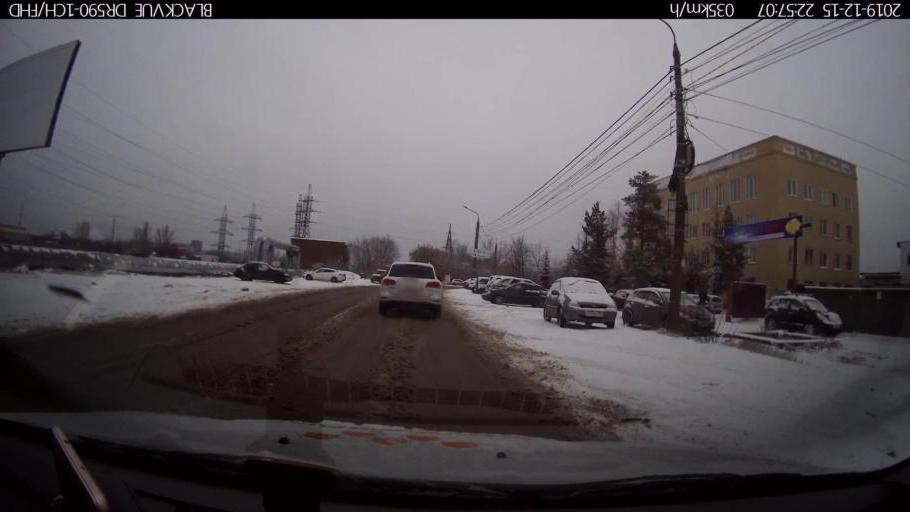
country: RU
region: Nizjnij Novgorod
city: Neklyudovo
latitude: 56.3464
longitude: 43.8911
